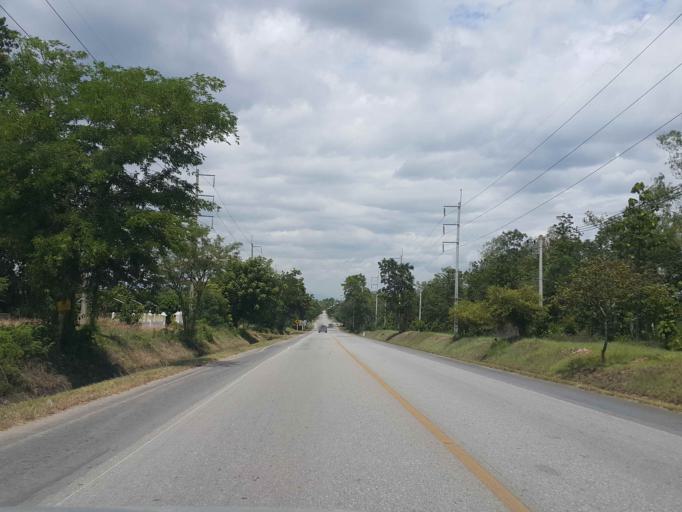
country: TH
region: Lamphun
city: Ban Hong
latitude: 18.3708
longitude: 98.8136
